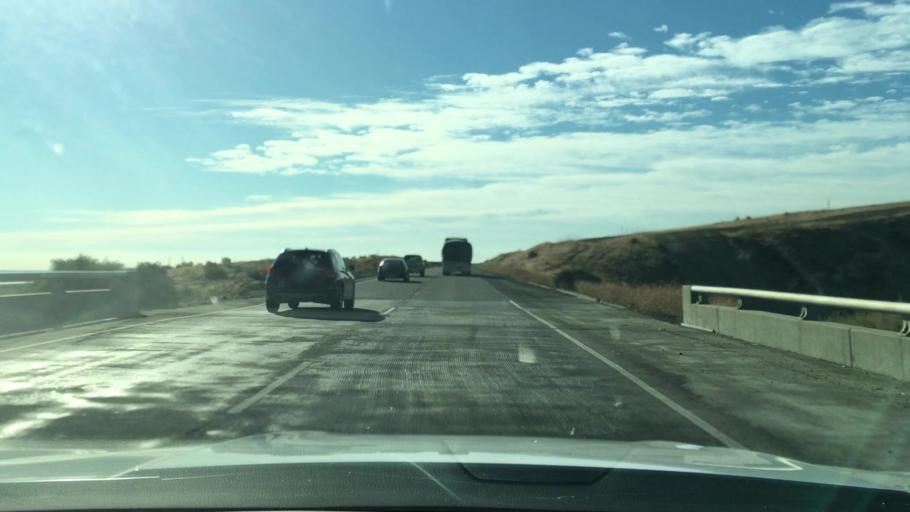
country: US
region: California
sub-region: Fresno County
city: Mendota
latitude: 36.4976
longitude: -120.4516
